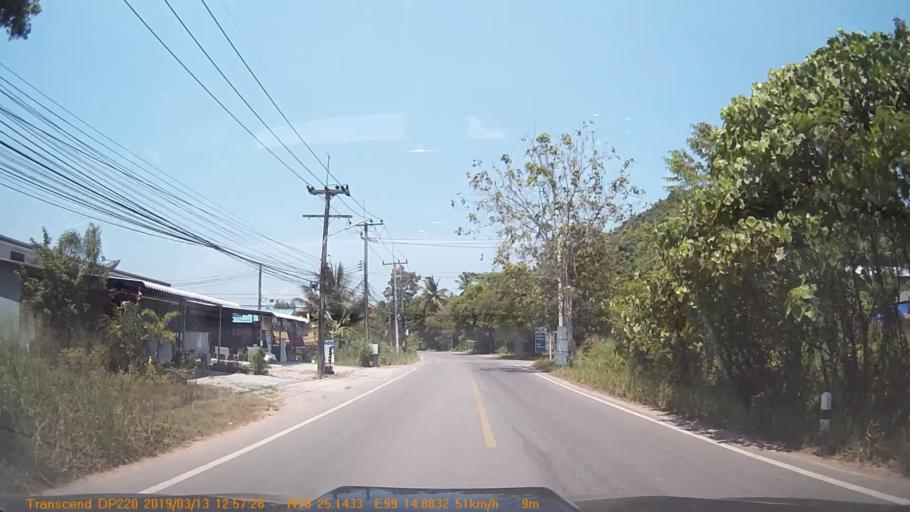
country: TH
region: Chumphon
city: Chumphon
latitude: 10.4193
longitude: 99.2481
